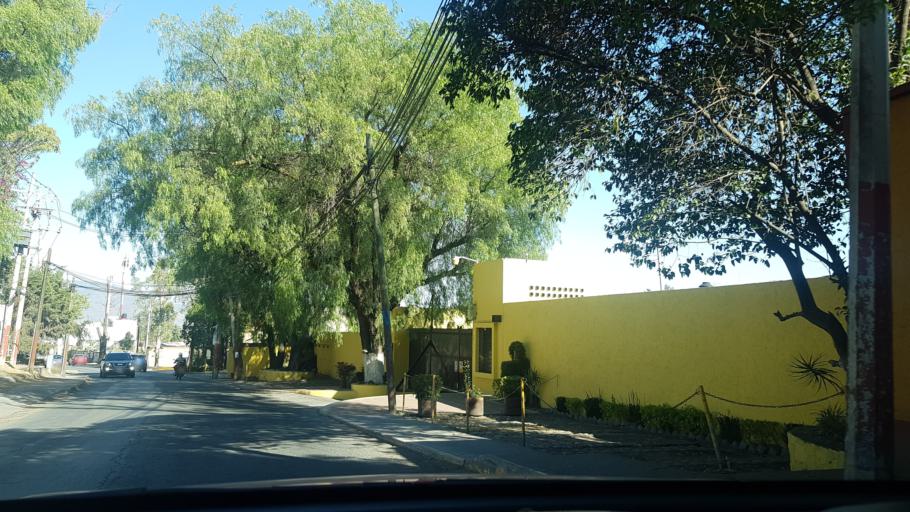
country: MX
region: Mexico
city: Cuautitlan Izcalli
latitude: 19.6234
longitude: -99.2274
